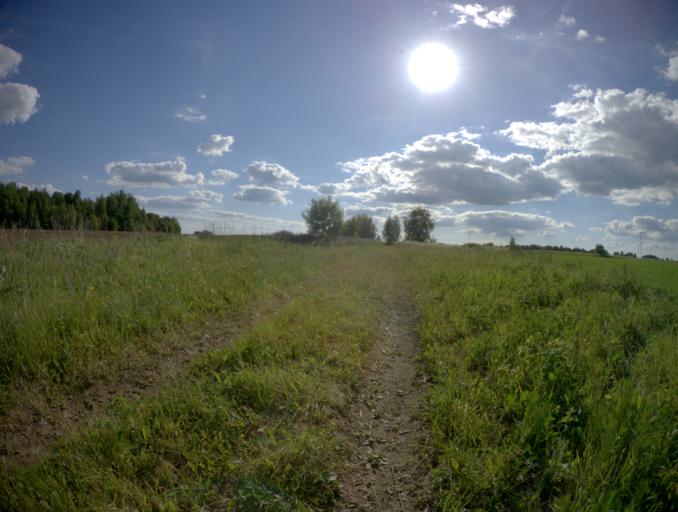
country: RU
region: Vladimir
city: Vladimir
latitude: 56.2872
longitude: 40.2858
